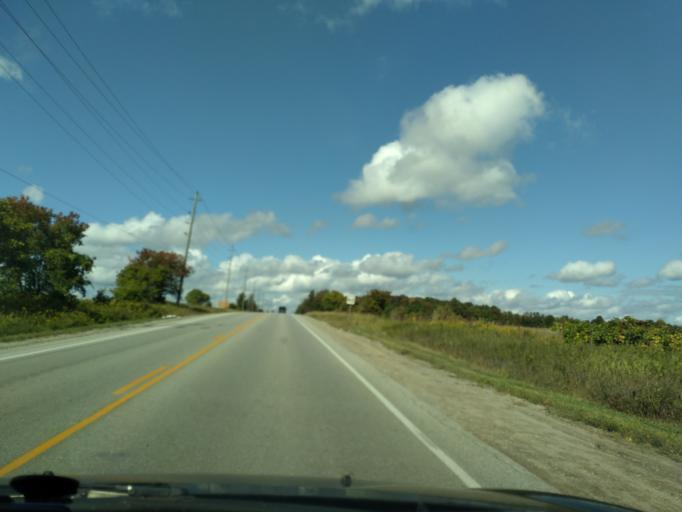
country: CA
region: Ontario
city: Innisfil
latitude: 44.2848
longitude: -79.5707
